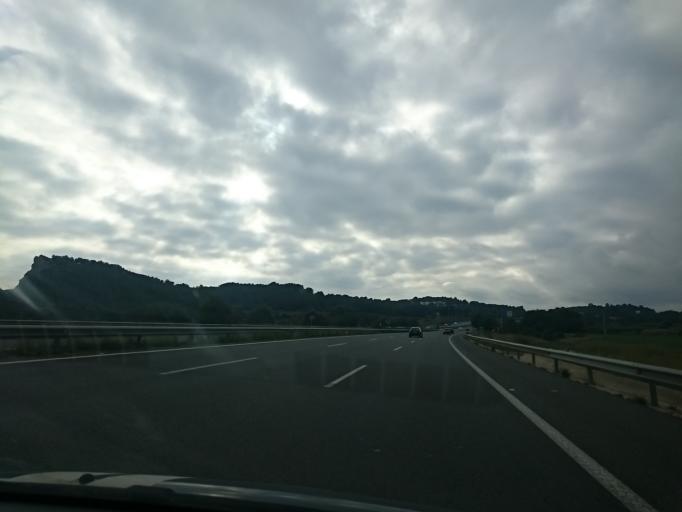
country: ES
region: Catalonia
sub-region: Provincia de Barcelona
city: Sant Pere de Ribes
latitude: 41.2439
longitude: 1.7748
